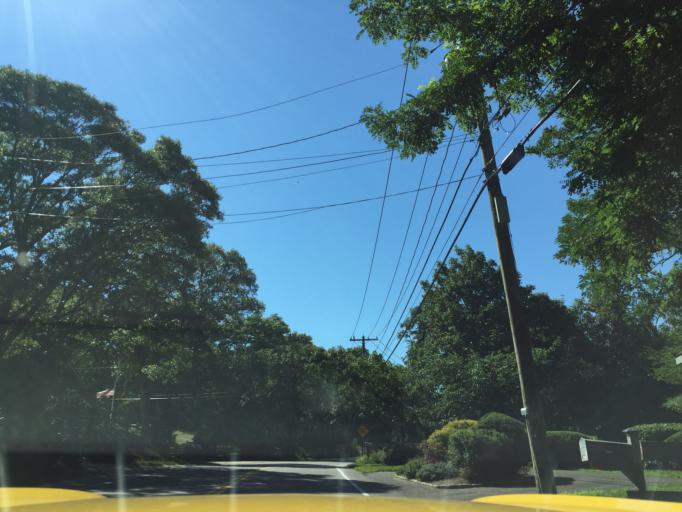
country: US
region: New York
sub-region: Suffolk County
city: Noyack
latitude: 40.9948
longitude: -72.3337
